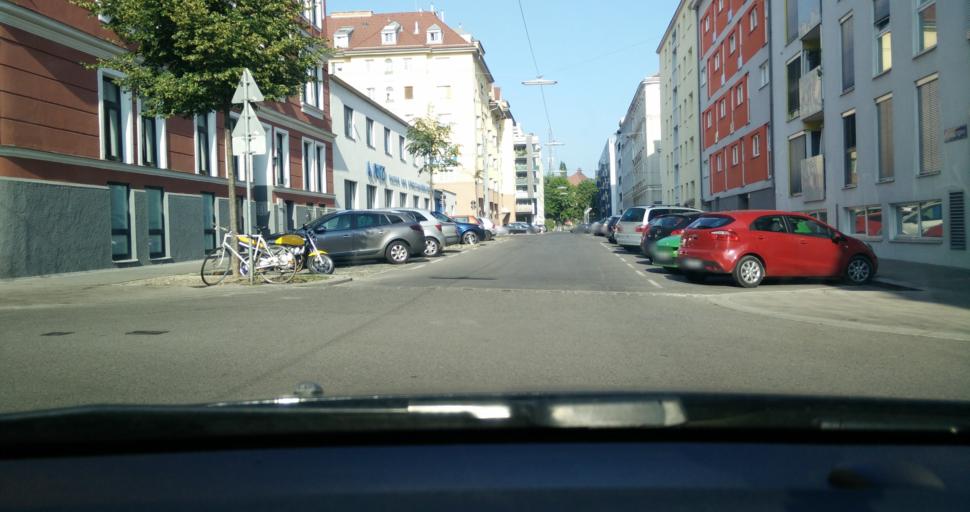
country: AT
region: Vienna
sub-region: Wien Stadt
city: Vienna
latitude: 48.2193
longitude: 16.3157
